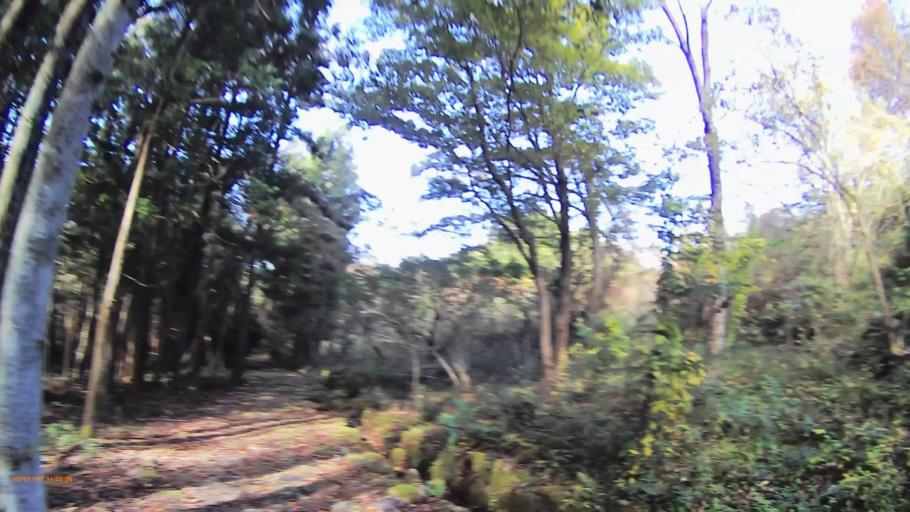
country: JP
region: Gifu
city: Mizunami
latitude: 35.4351
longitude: 137.2797
